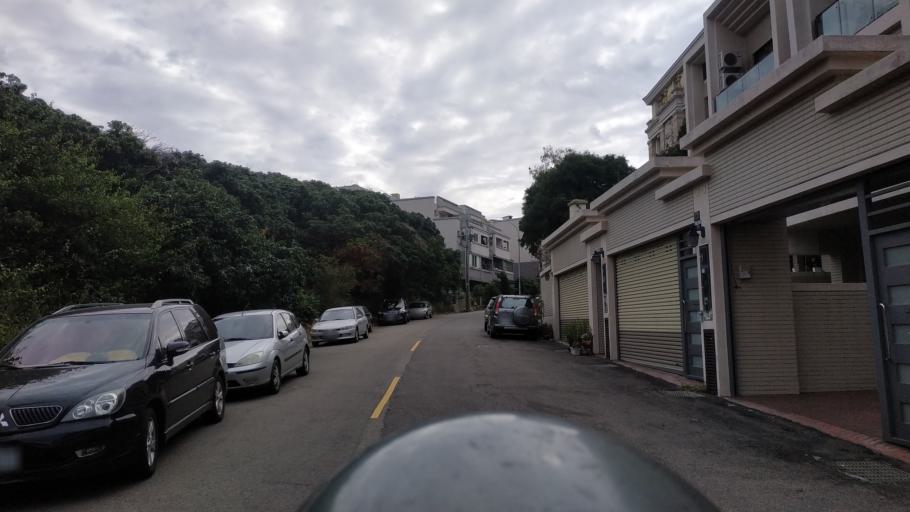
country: TW
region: Taiwan
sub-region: Taichung City
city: Taichung
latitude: 24.2141
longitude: 120.5766
